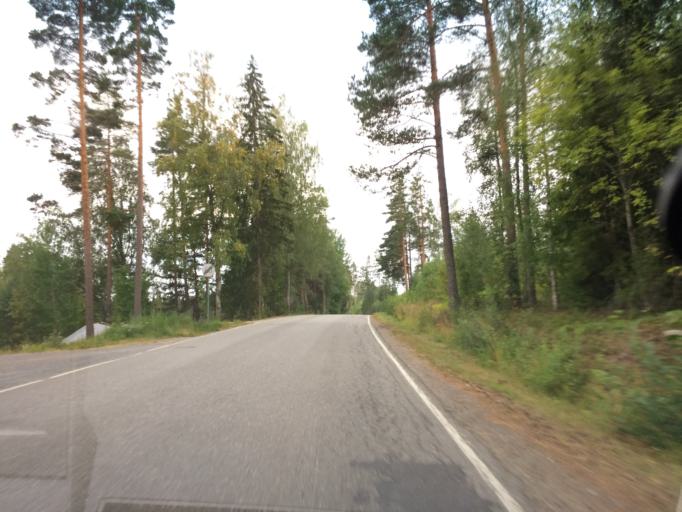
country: FI
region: Pirkanmaa
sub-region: Tampere
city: Luopioinen
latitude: 61.2435
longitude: 24.7095
